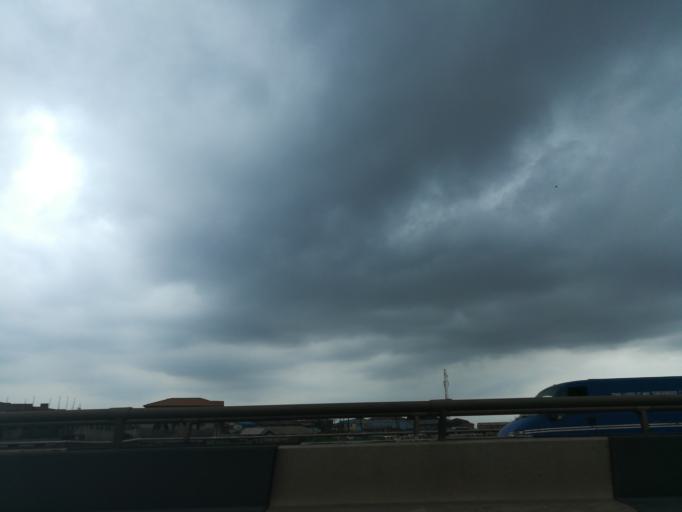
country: NG
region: Lagos
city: Somolu
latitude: 6.5404
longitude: 3.3997
